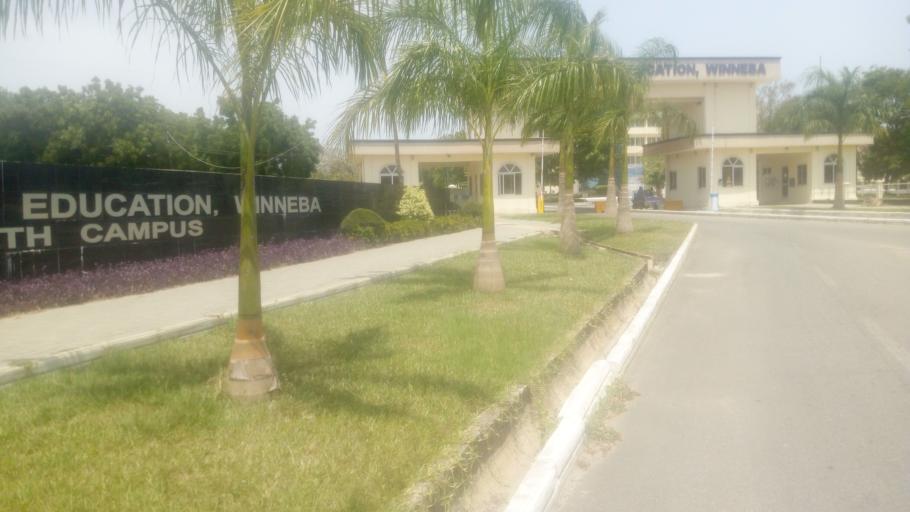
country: GH
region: Central
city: Winneba
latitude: 5.3621
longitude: -0.6343
